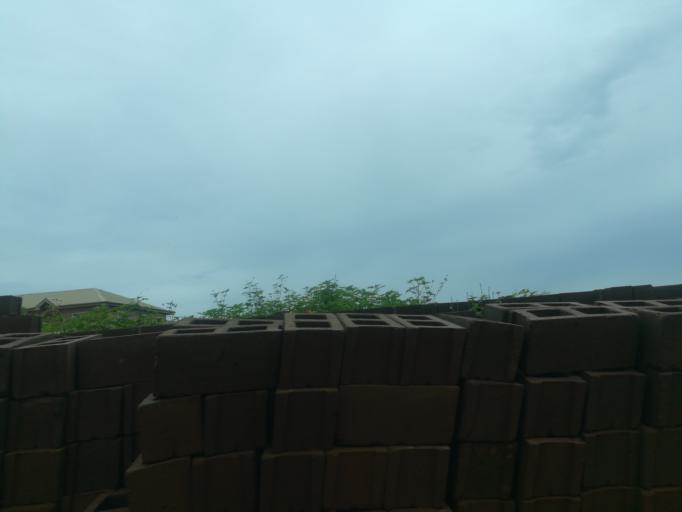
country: NG
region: Oyo
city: Ibadan
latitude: 7.3198
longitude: 3.8843
